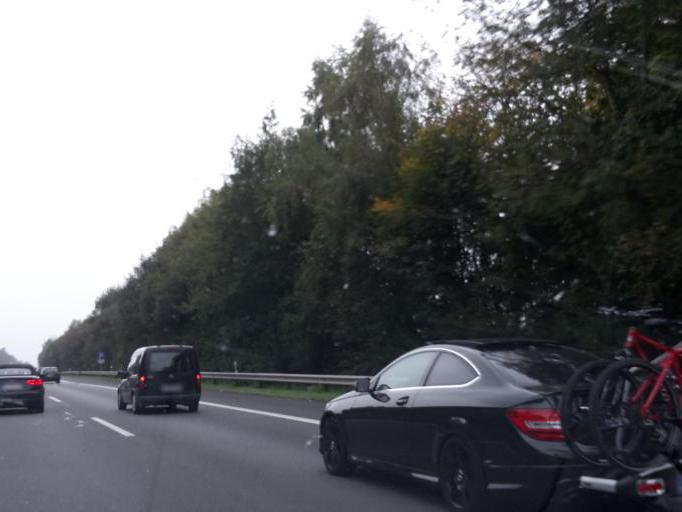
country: DE
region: Lower Saxony
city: Neuenkirchen
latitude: 52.5182
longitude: 8.1020
